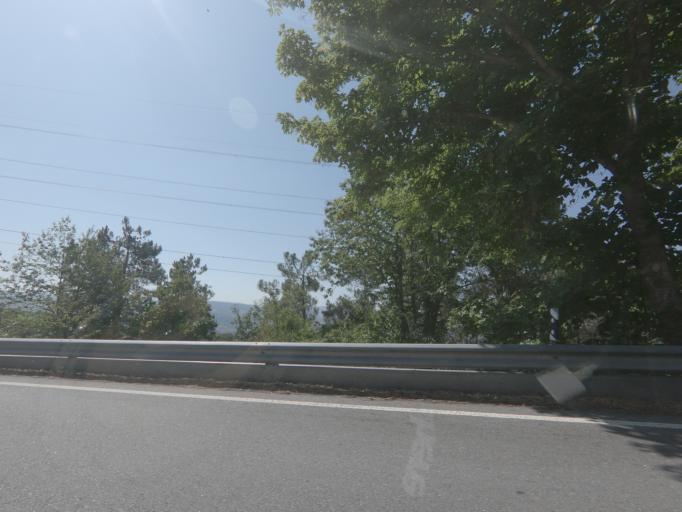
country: PT
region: Viseu
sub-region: Tarouca
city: Tarouca
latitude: 41.0397
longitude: -7.7411
